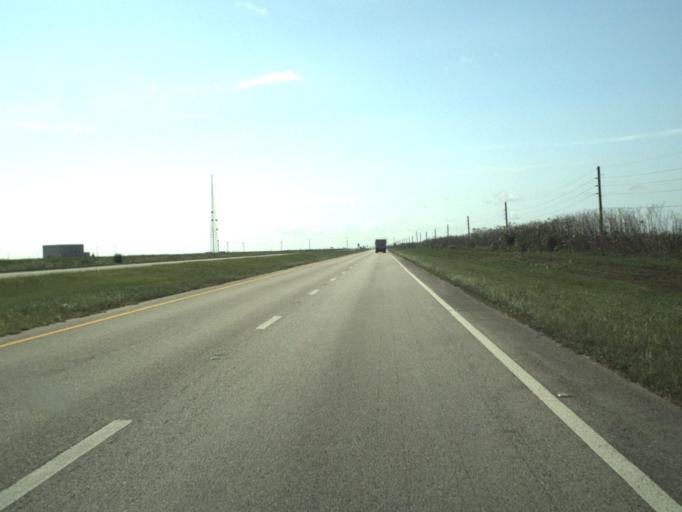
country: US
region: Florida
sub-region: Palm Beach County
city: Belle Glade Camp
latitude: 26.4410
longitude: -80.6201
